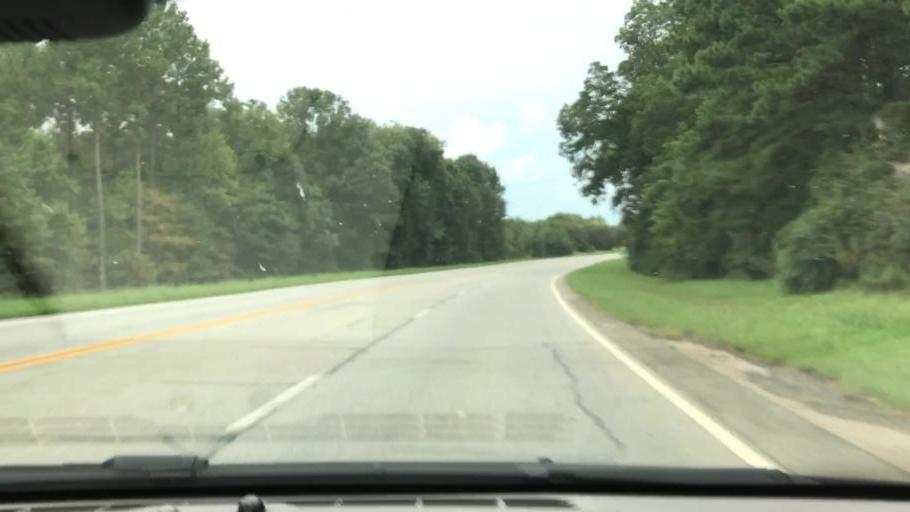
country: US
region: Georgia
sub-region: Early County
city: Blakely
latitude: 31.3323
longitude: -84.9934
